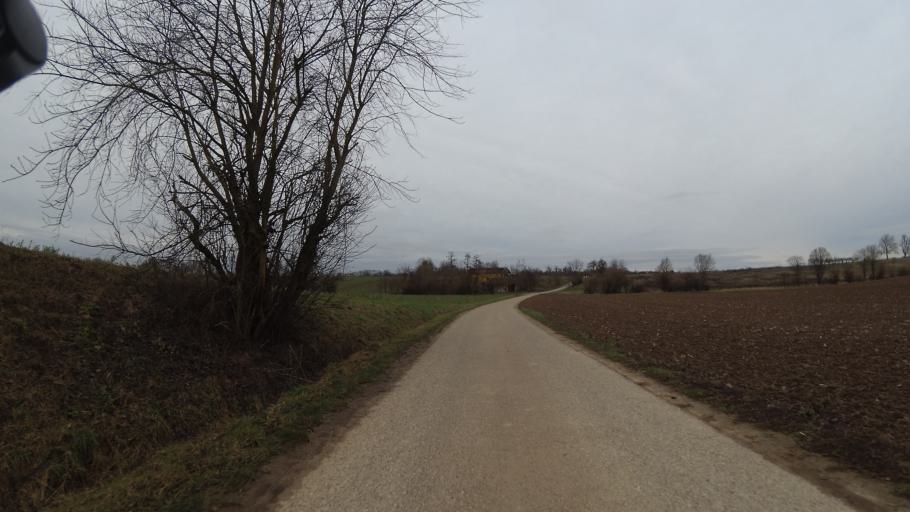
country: DE
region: Baden-Wuerttemberg
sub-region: Regierungsbezirk Stuttgart
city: Oedheim
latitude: 49.2247
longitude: 9.2502
